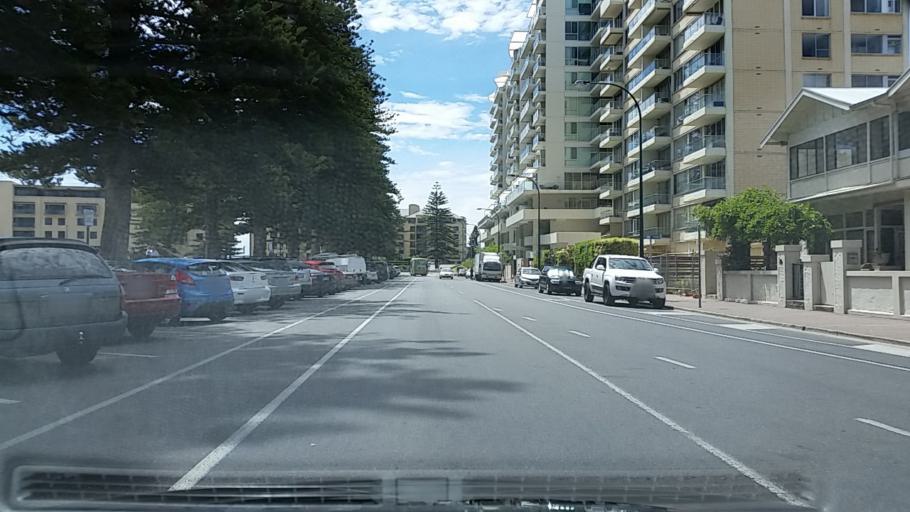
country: AU
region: South Australia
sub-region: Adelaide
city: Glenelg
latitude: -34.9784
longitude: 138.5123
